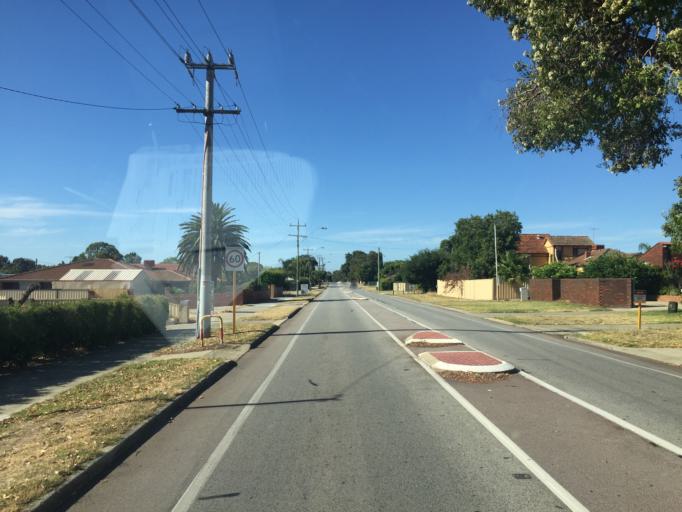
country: AU
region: Western Australia
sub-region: Gosnells
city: Maddington
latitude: -32.0393
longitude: 115.9820
